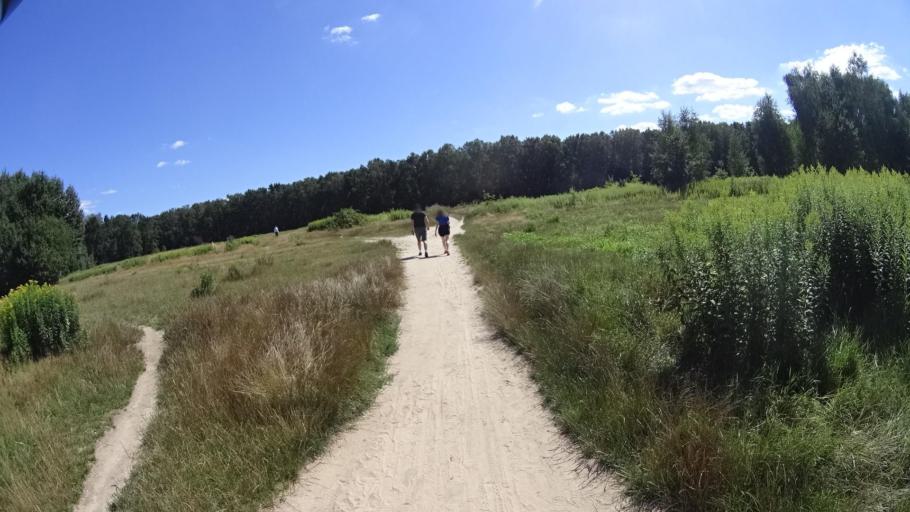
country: PL
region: Masovian Voivodeship
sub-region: Warszawa
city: Kabaty
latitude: 52.1258
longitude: 21.0757
